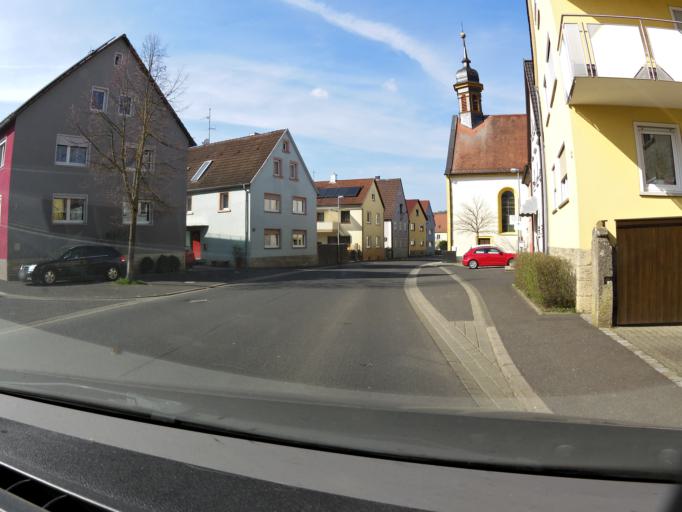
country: DE
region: Bavaria
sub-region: Regierungsbezirk Unterfranken
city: Bieberehren
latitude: 49.5143
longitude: 10.0083
